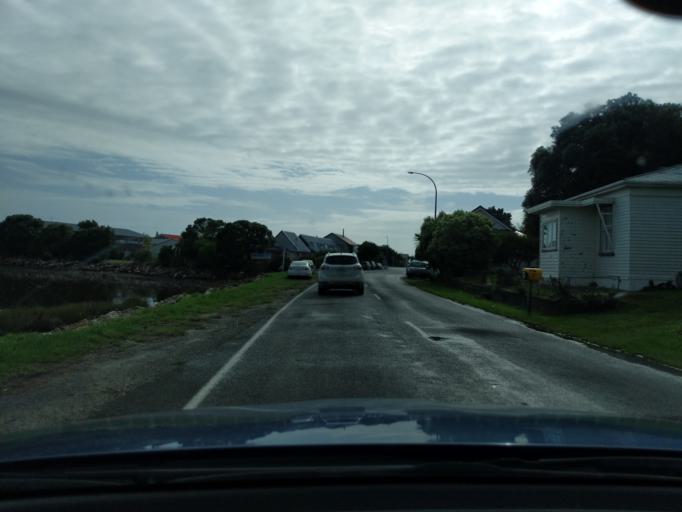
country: NZ
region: Tasman
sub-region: Tasman District
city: Takaka
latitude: -40.6780
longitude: 172.6812
